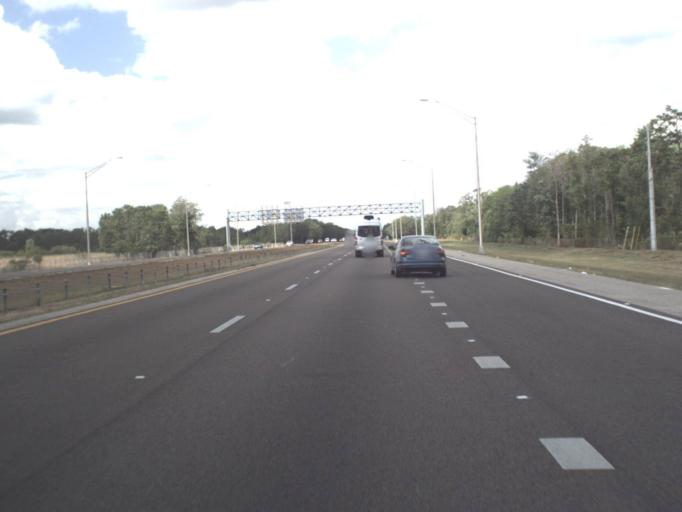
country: US
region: Florida
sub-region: Orange County
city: Wedgefield
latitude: 28.4521
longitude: -81.0634
